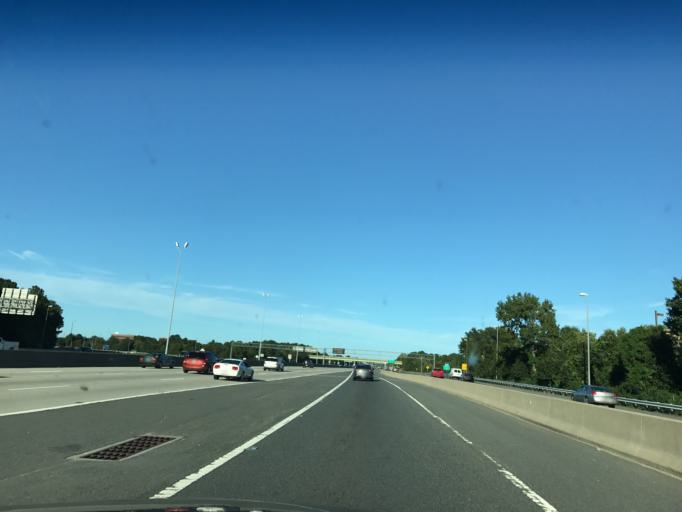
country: US
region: Virginia
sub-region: City of Chesapeake
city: Chesapeake
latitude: 36.7817
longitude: -76.2389
